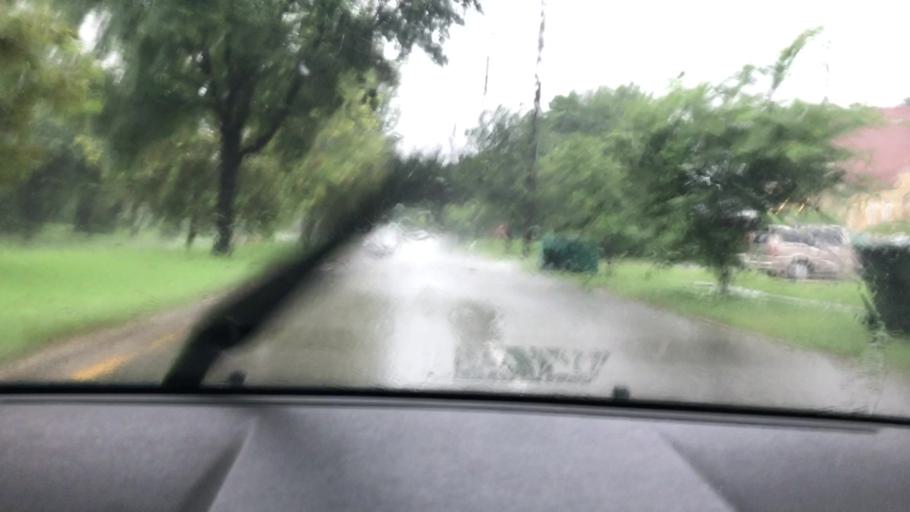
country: US
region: Virginia
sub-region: City of Richmond
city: Richmond
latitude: 37.5741
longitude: -77.4455
